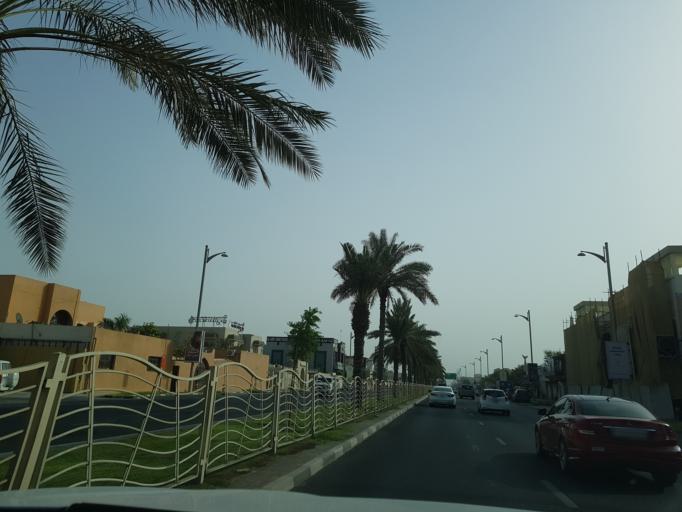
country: AE
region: Dubai
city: Dubai
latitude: 25.1785
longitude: 55.2228
